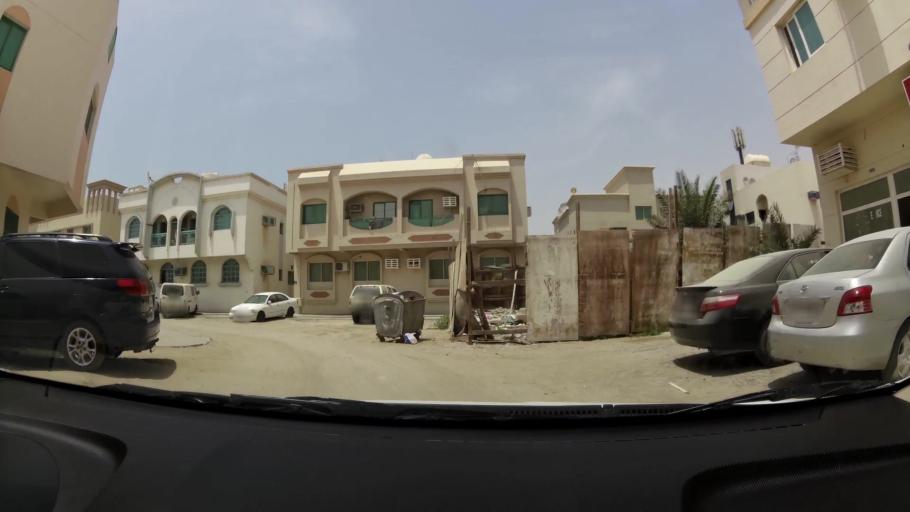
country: AE
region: Ash Shariqah
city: Sharjah
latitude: 25.3529
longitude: 55.4042
